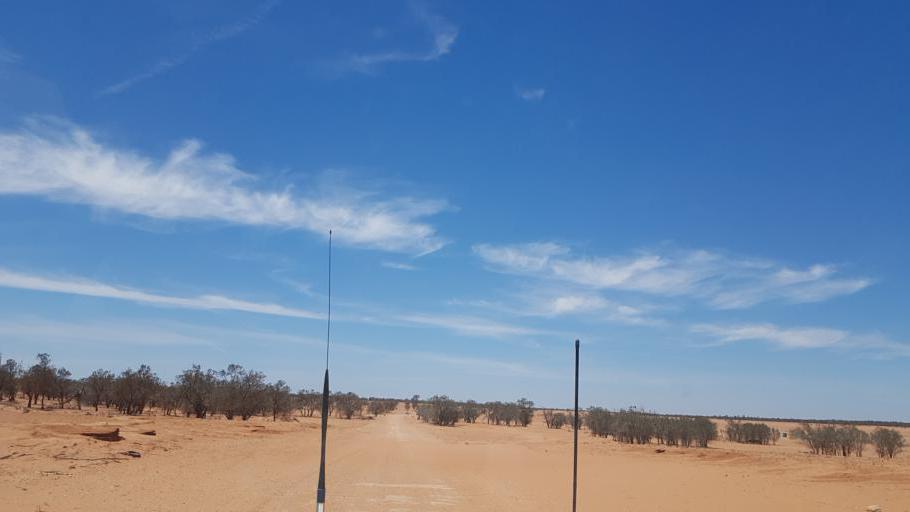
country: AU
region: New South Wales
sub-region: Wentworth
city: Dareton
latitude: -33.3464
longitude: 141.4610
